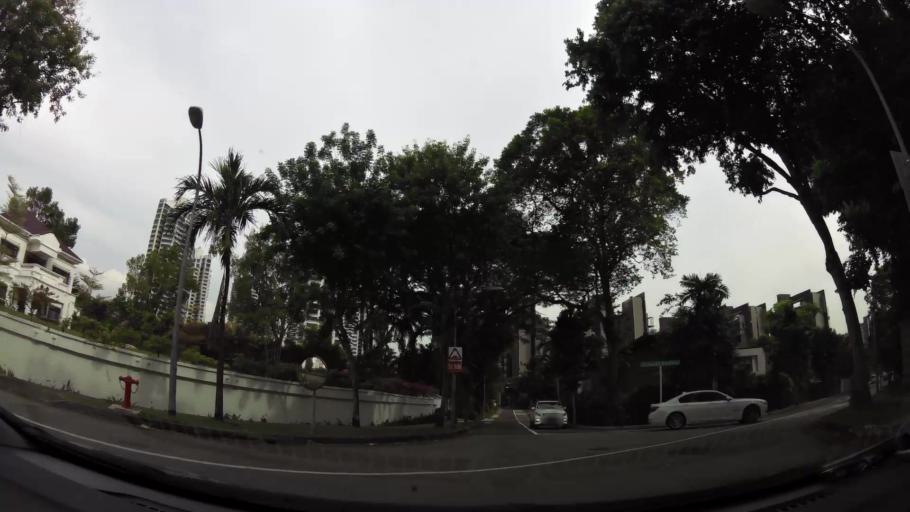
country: SG
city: Singapore
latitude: 1.3152
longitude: 103.8001
